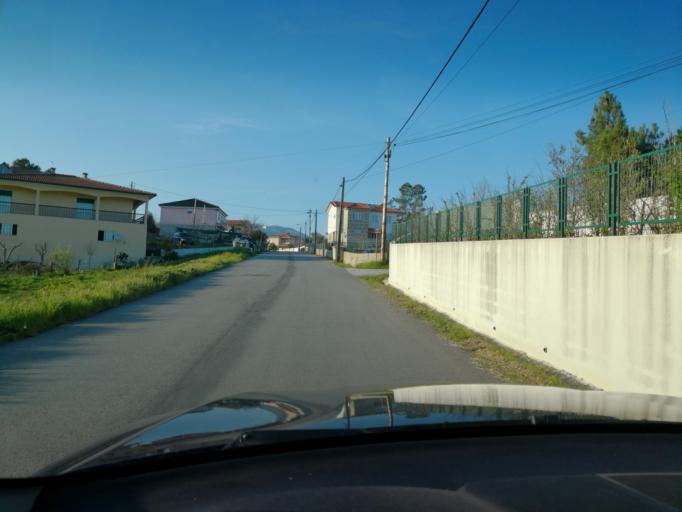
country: PT
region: Vila Real
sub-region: Vila Real
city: Vila Real
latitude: 41.2954
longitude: -7.7659
